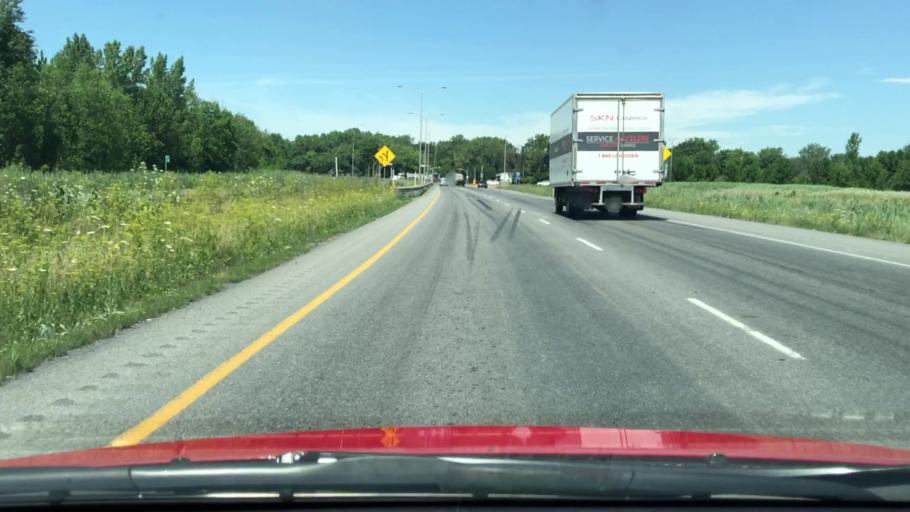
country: CA
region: Quebec
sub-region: Monteregie
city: Saint-Constant
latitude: 45.3925
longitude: -73.6036
